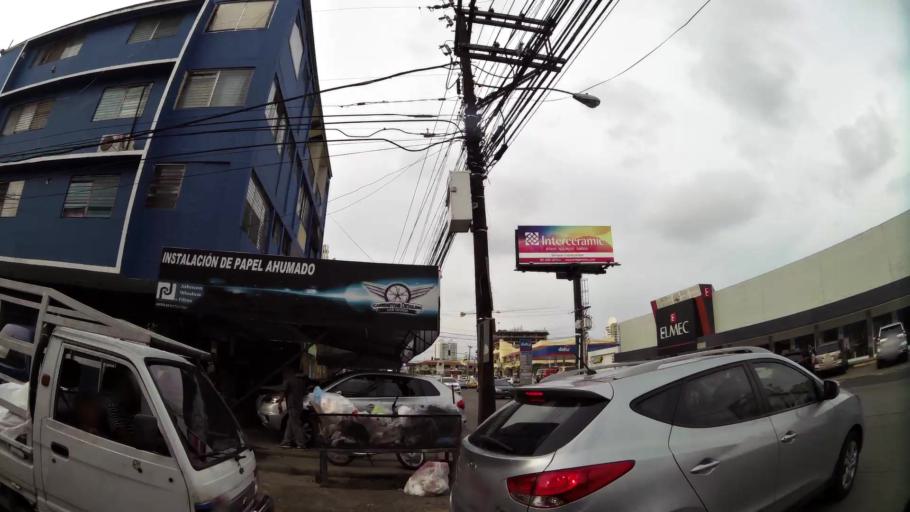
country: PA
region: Panama
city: Panama
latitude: 9.0004
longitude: -79.5201
